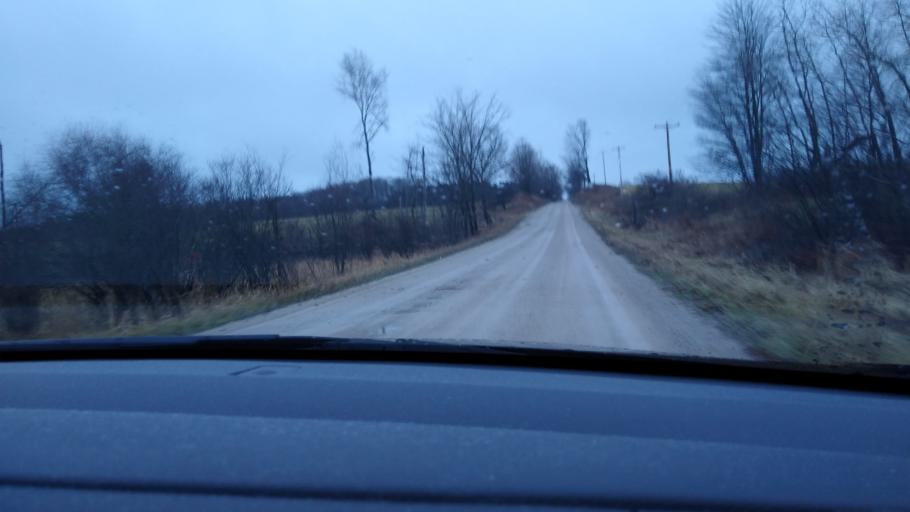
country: US
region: Michigan
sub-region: Wexford County
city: Cadillac
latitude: 44.1729
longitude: -85.3953
